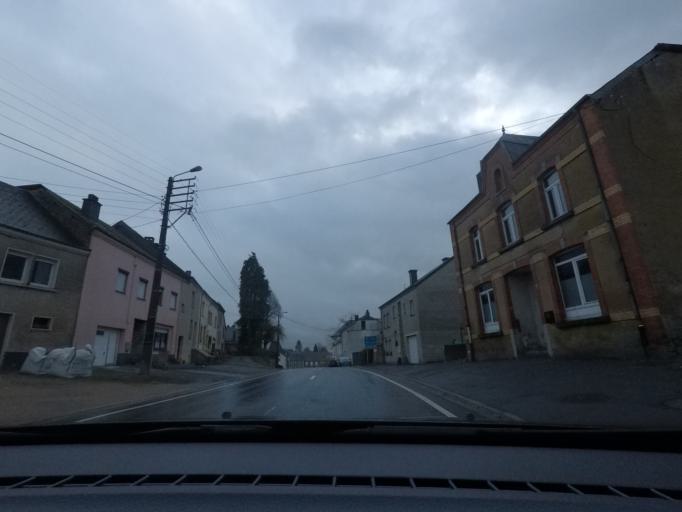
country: BE
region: Wallonia
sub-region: Province du Luxembourg
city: Tintigny
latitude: 49.7188
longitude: 5.4860
